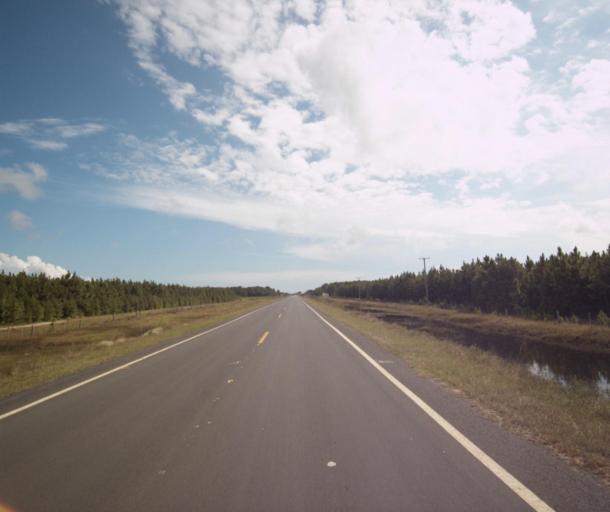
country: BR
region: Rio Grande do Sul
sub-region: Sao Lourenco Do Sul
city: Sao Lourenco do Sul
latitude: -31.5971
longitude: -51.3759
